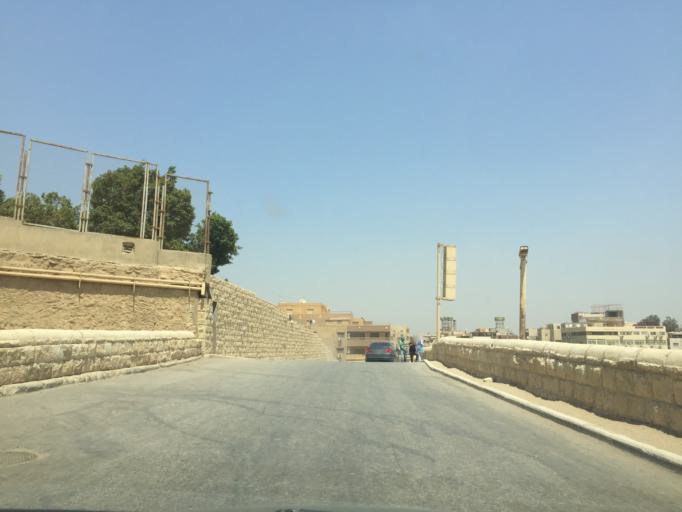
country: EG
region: Al Jizah
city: Al Jizah
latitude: 29.9758
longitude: 31.1388
